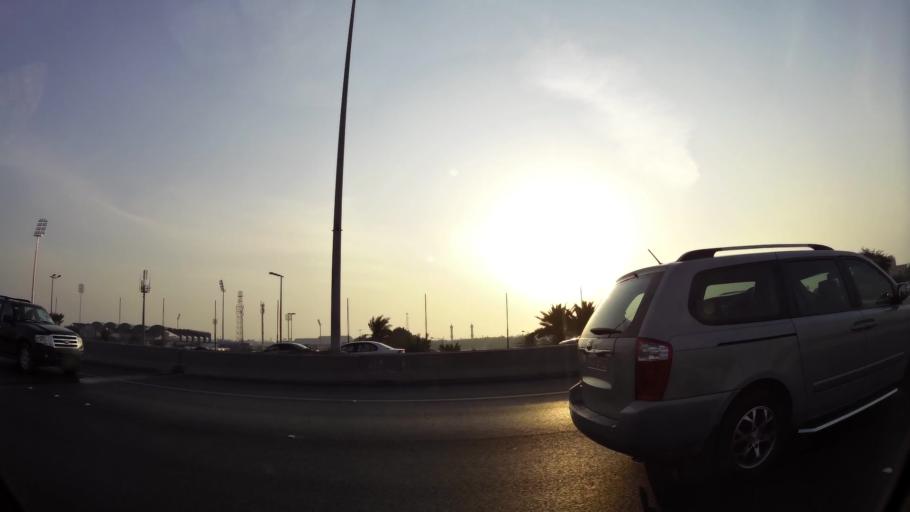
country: KW
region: Muhafazat Hawalli
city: Salwa
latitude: 29.2940
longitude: 48.0692
